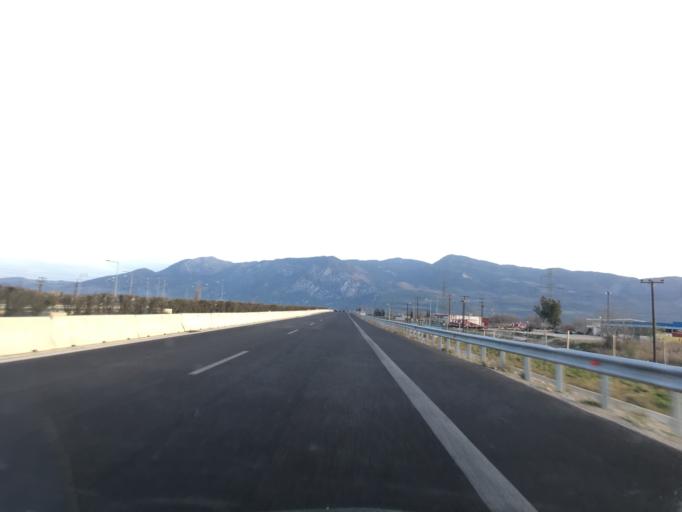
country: GR
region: Central Greece
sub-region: Nomos Fthiotidos
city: Anthili
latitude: 38.8587
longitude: 22.4636
